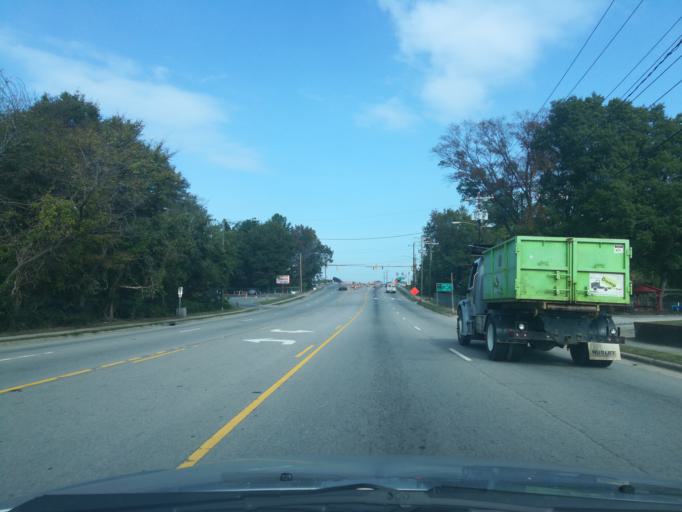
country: US
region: North Carolina
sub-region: Durham County
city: Durham
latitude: 35.9802
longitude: -78.8914
